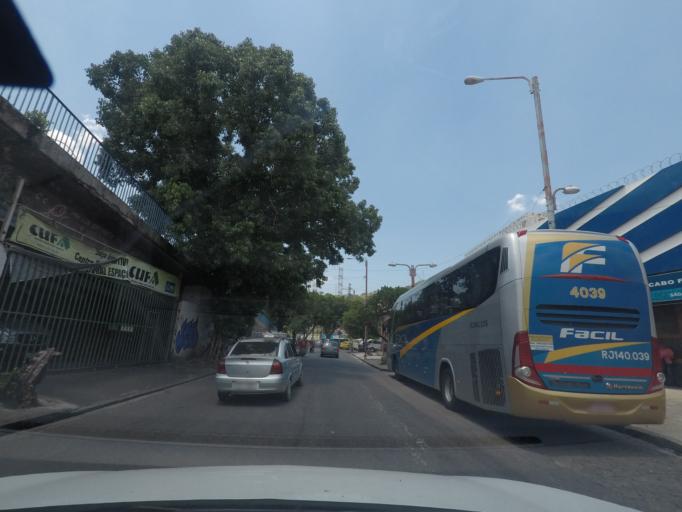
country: BR
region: Rio de Janeiro
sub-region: Sao Joao De Meriti
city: Sao Joao de Meriti
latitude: -22.8772
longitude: -43.3354
